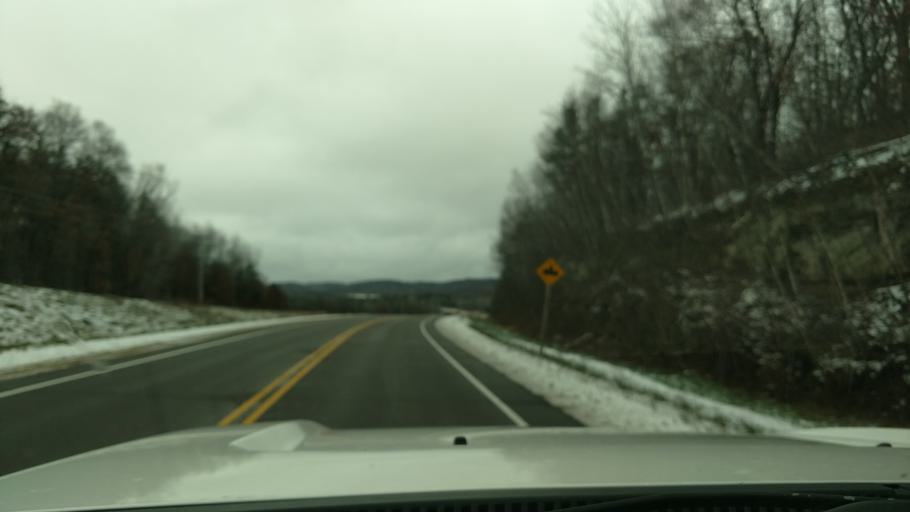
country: US
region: Wisconsin
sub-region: Dunn County
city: Tainter Lake
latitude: 45.1248
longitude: -91.9020
